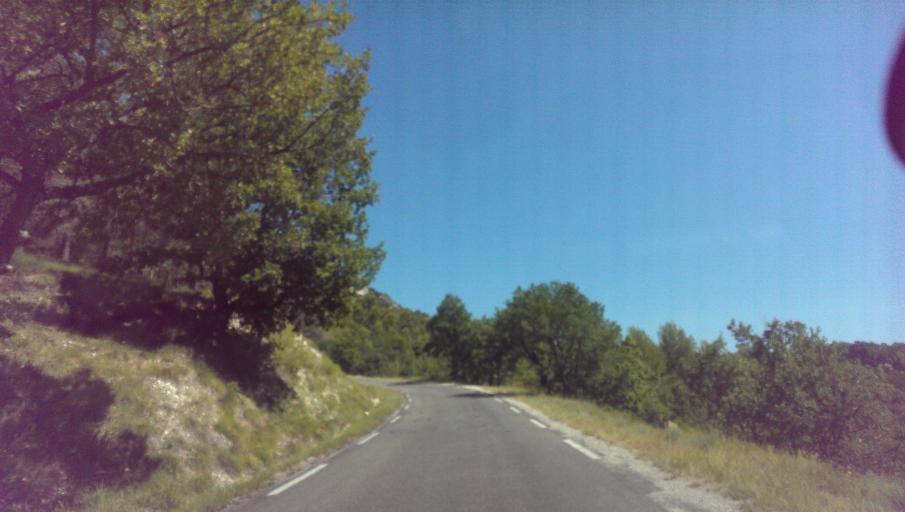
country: FR
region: Provence-Alpes-Cote d'Azur
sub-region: Departement du Vaucluse
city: Gordes
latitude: 43.9344
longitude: 5.1883
